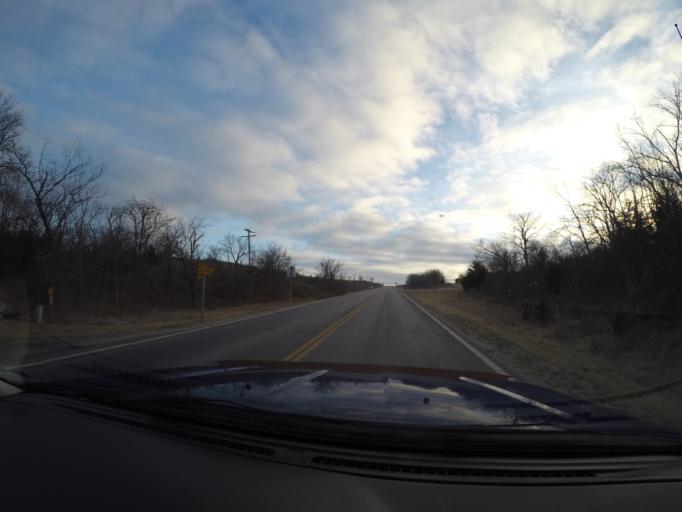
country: US
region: Kansas
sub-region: Morris County
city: Council Grove
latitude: 38.6508
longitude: -96.4887
